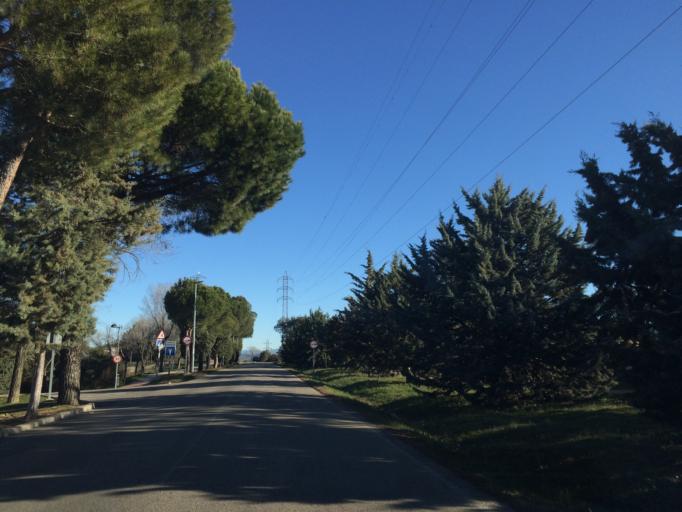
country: ES
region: Madrid
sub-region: Provincia de Madrid
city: Tres Cantos
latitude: 40.6040
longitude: -3.6892
